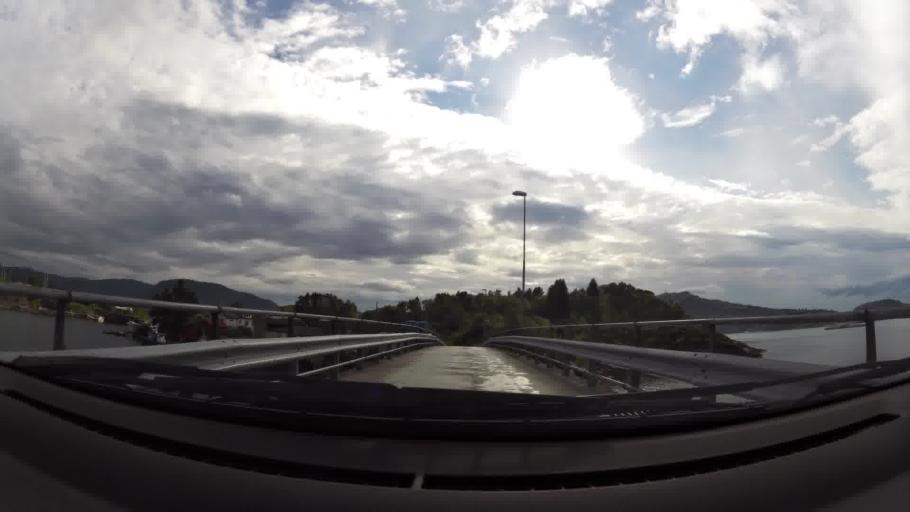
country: NO
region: More og Romsdal
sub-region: Kristiansund
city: Kristiansund
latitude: 63.0617
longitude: 7.7016
